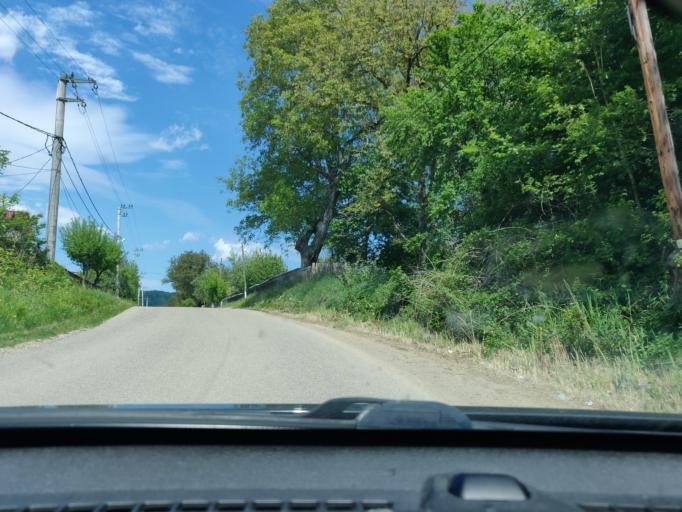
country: RO
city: Vizantea-Manastireasca
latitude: 45.9804
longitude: 26.7981
